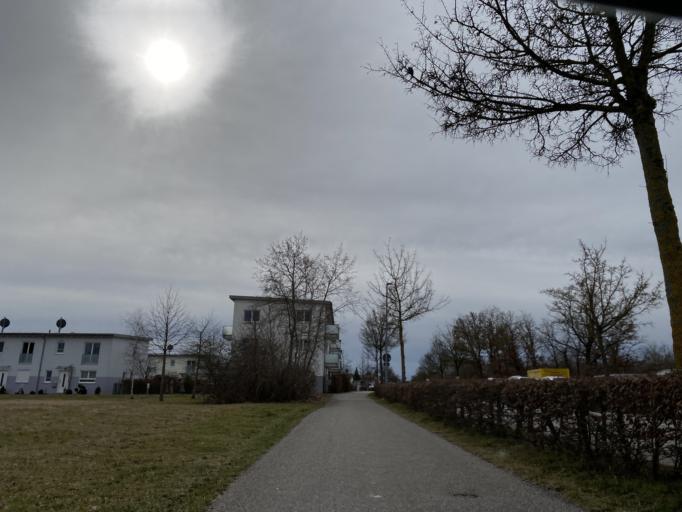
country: DE
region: Bavaria
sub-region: Upper Bavaria
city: Fuerstenfeldbruck
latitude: 48.1697
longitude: 11.2268
